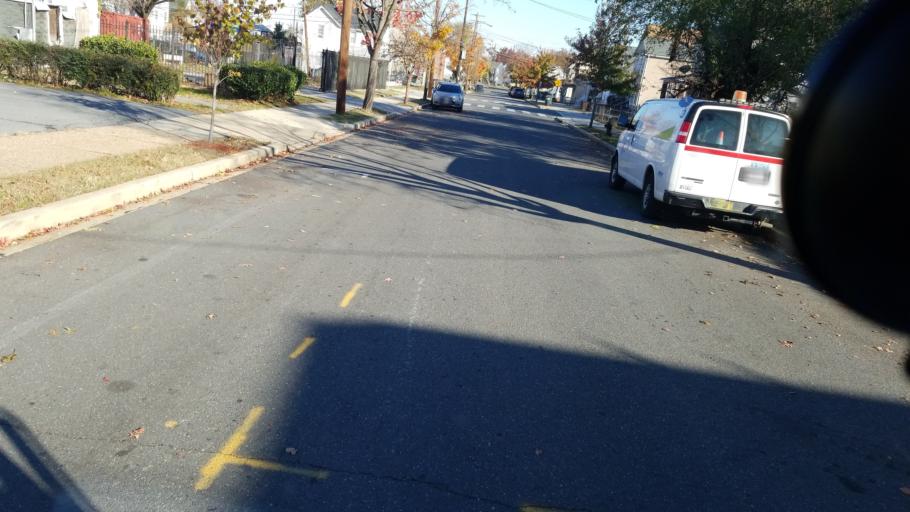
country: US
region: Maryland
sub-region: Prince George's County
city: Fairmount Heights
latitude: 38.9041
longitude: -76.9364
